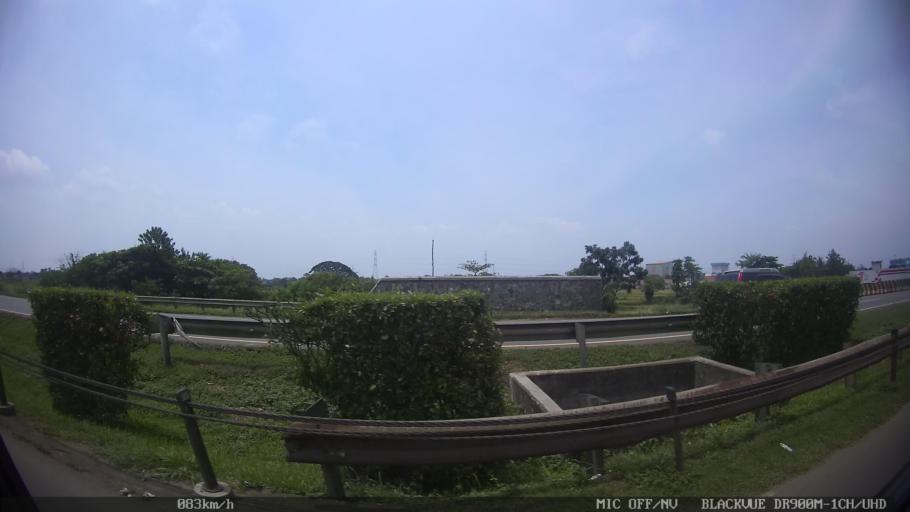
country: ID
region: West Java
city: Kresek
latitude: -6.1628
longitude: 106.3313
